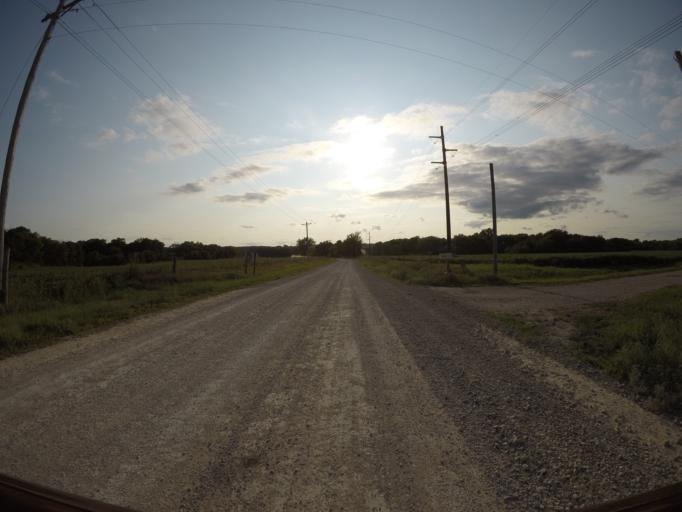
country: US
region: Kansas
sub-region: Wabaunsee County
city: Alma
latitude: 38.9928
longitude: -96.2722
